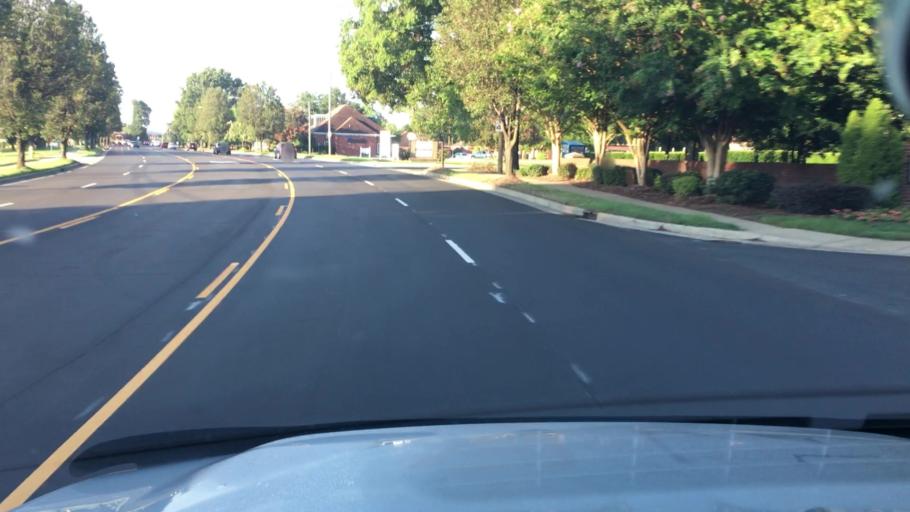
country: US
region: North Carolina
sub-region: Mecklenburg County
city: Pineville
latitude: 35.0919
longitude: -80.8443
